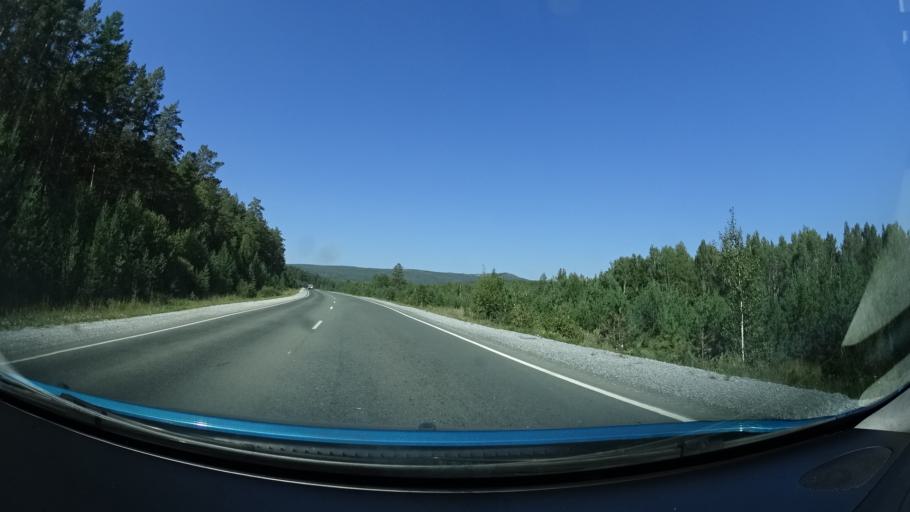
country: RU
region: Bashkortostan
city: Abzakovo
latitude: 53.8560
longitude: 58.5725
